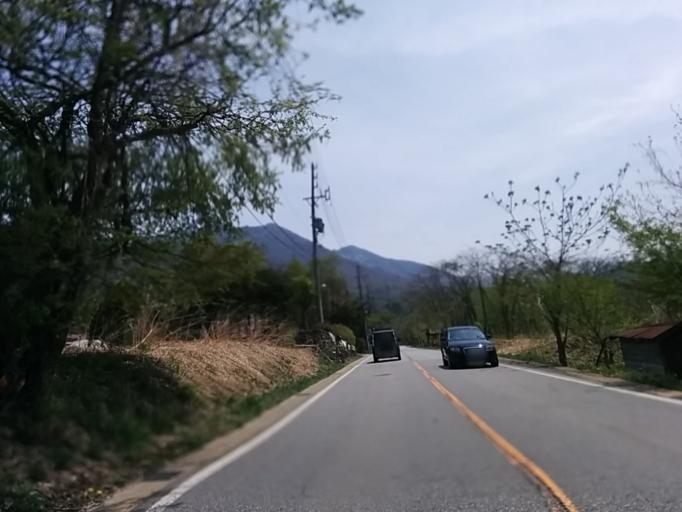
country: JP
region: Gifu
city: Takayama
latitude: 36.2240
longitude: 137.5351
